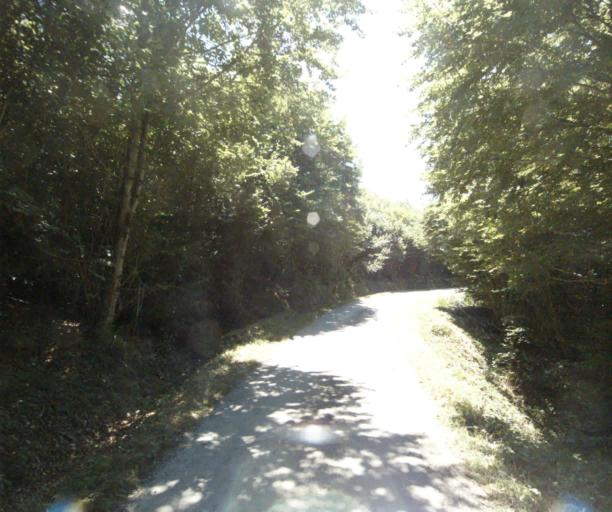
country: FR
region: Midi-Pyrenees
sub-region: Departement du Tarn
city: Dourgne
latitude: 43.4494
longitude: 2.2087
